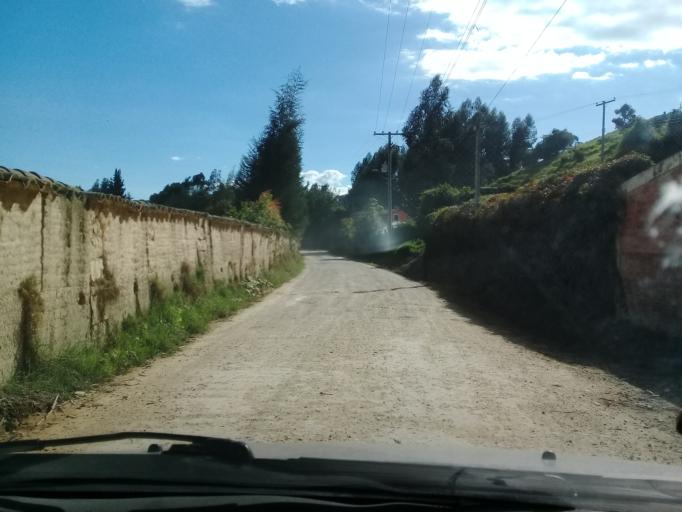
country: CO
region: Cundinamarca
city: Tabio
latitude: 4.9653
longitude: -74.0795
